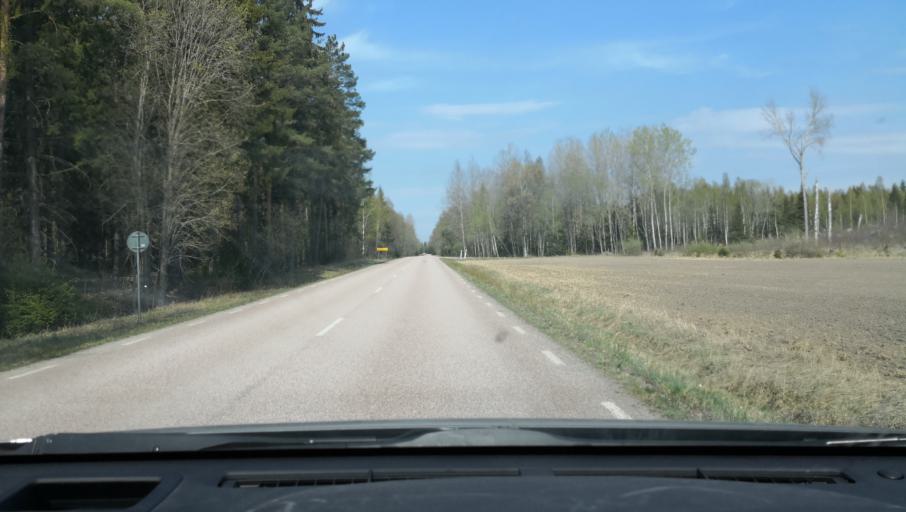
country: SE
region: Vaestmanland
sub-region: Vasteras
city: Skultuna
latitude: 59.7482
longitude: 16.4104
